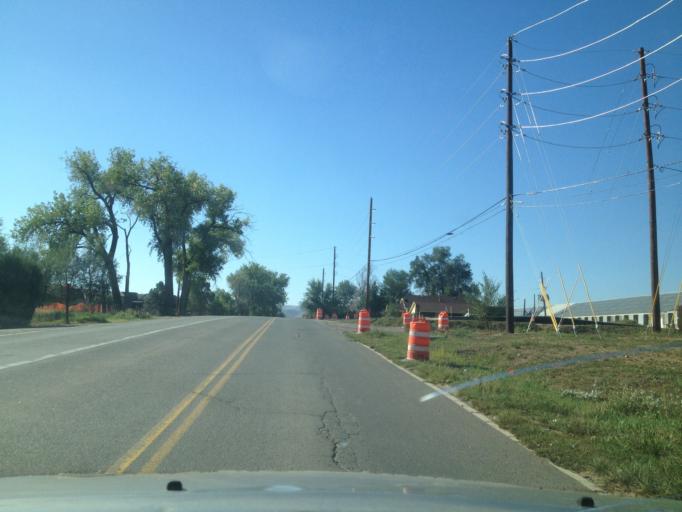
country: US
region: Colorado
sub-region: Jefferson County
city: Applewood
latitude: 39.7984
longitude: -105.1747
